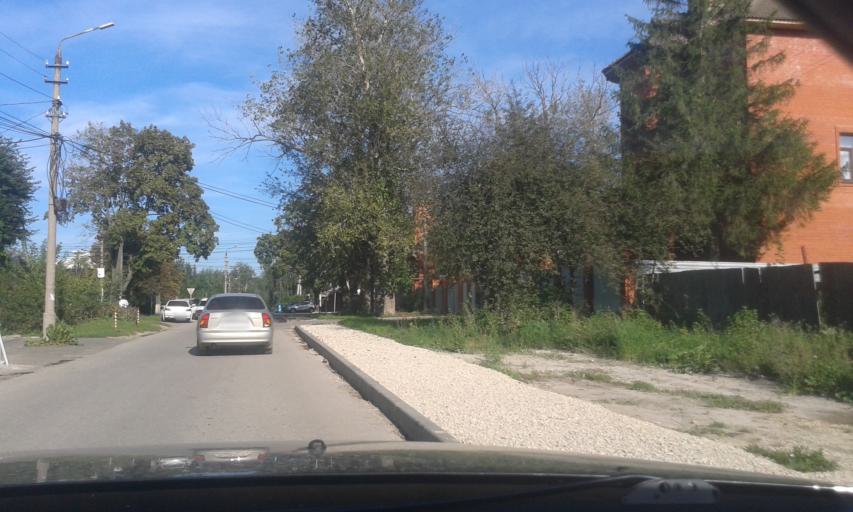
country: RU
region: Tula
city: Mendeleyevskiy
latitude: 54.1792
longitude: 37.5724
